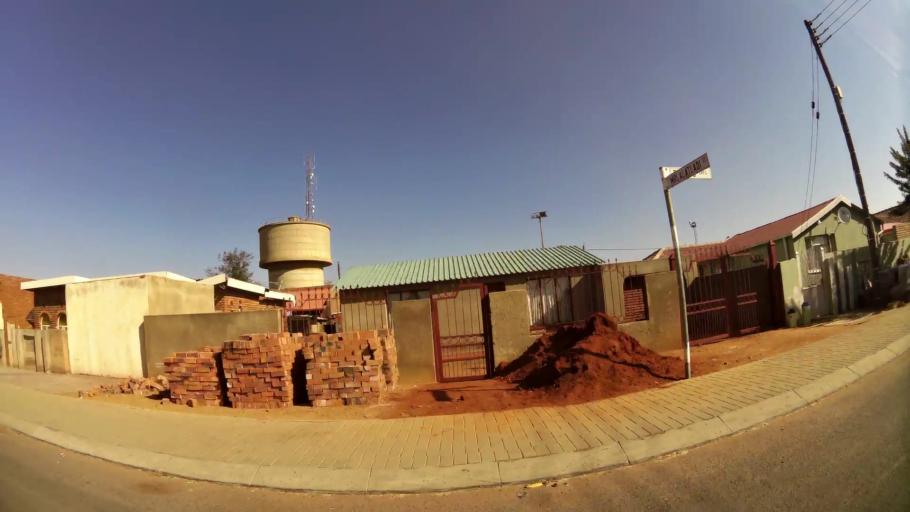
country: ZA
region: Gauteng
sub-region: City of Tshwane Metropolitan Municipality
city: Mabopane
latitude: -25.5352
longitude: 28.0990
